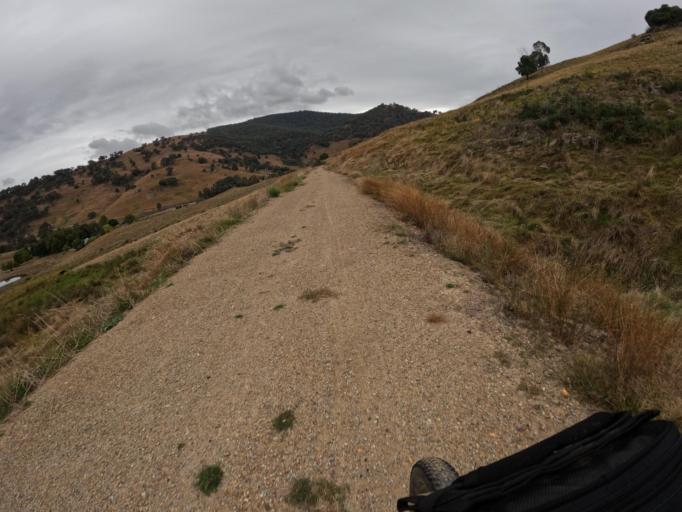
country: AU
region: New South Wales
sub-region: Albury Municipality
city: East Albury
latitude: -36.1844
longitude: 147.3672
